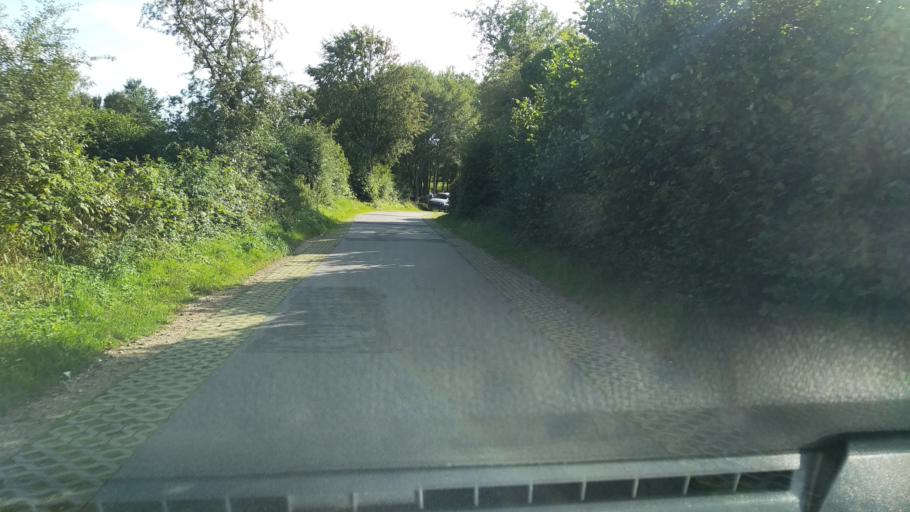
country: DE
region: Schleswig-Holstein
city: Busdorf
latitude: 54.4834
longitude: 9.5413
